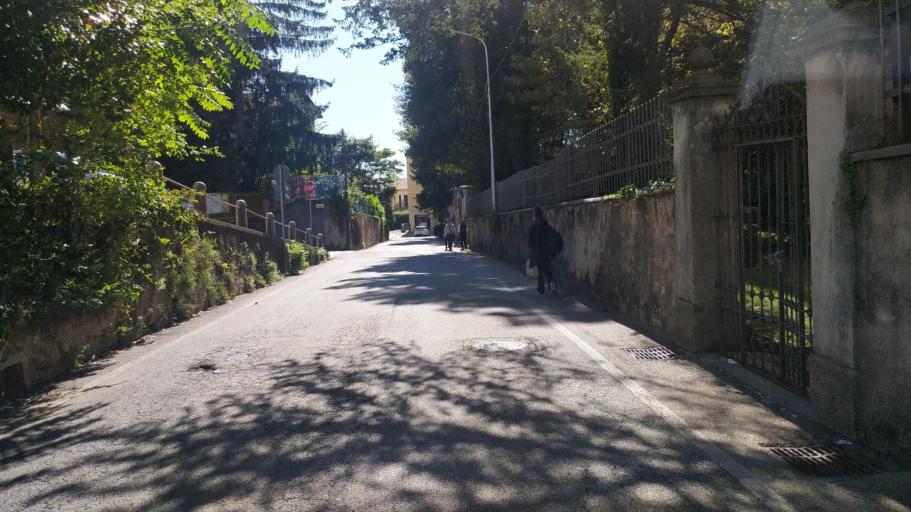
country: IT
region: Lombardy
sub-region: Provincia di Varese
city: Varese
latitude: 45.8164
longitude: 8.8137
